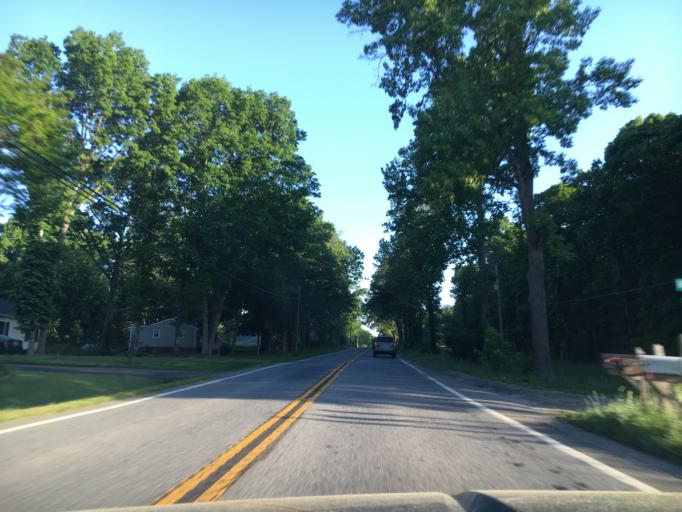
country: US
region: Virginia
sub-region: Campbell County
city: Rustburg
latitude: 37.2527
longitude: -79.1195
